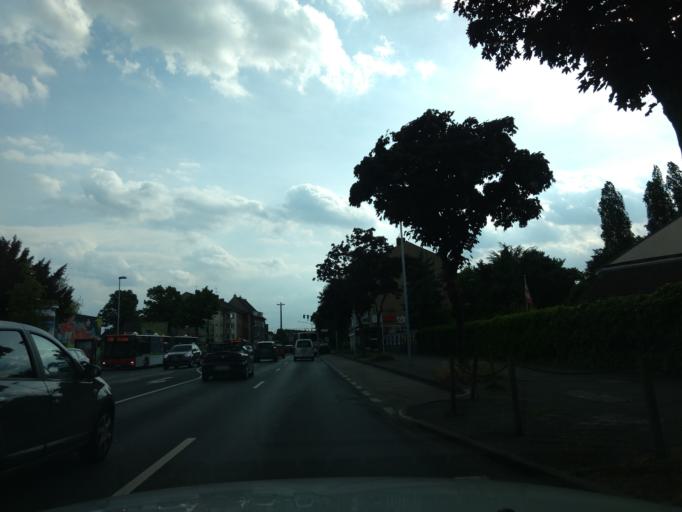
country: DE
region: North Rhine-Westphalia
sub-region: Regierungsbezirk Dusseldorf
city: Dusseldorf
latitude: 51.2756
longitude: 6.7848
